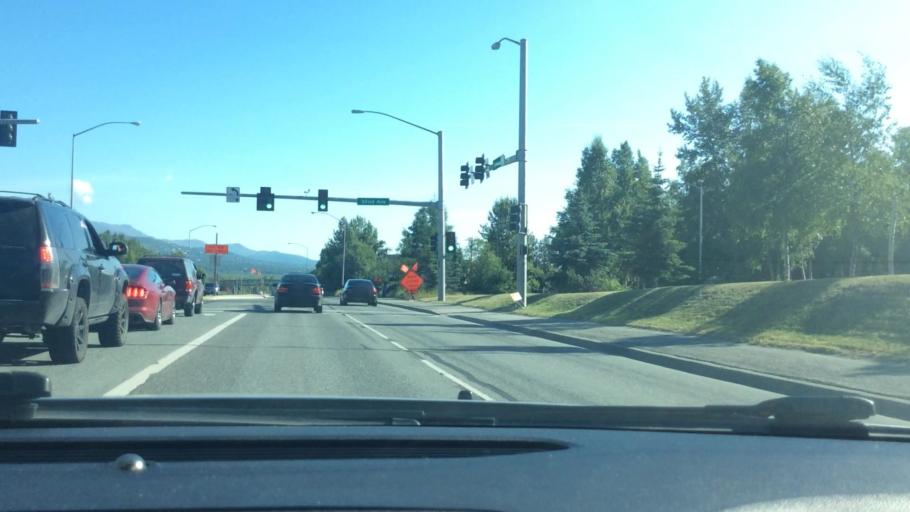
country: US
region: Alaska
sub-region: Anchorage Municipality
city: Elmendorf Air Force Base
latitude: 61.1923
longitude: -149.7335
